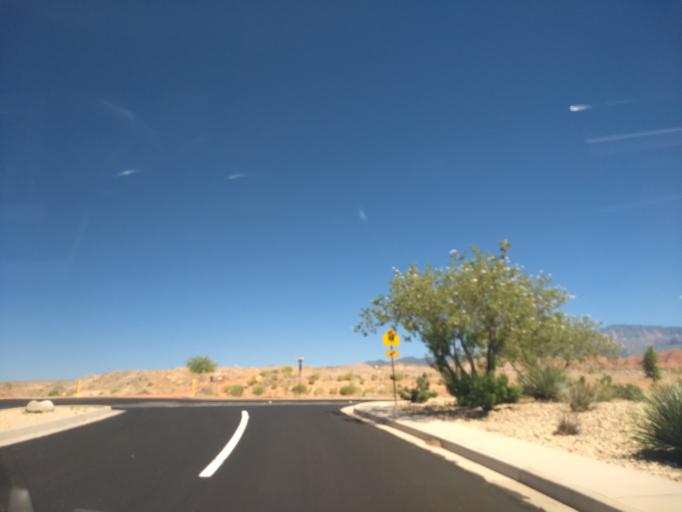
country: US
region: Utah
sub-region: Washington County
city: Washington
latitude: 37.1492
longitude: -113.4654
